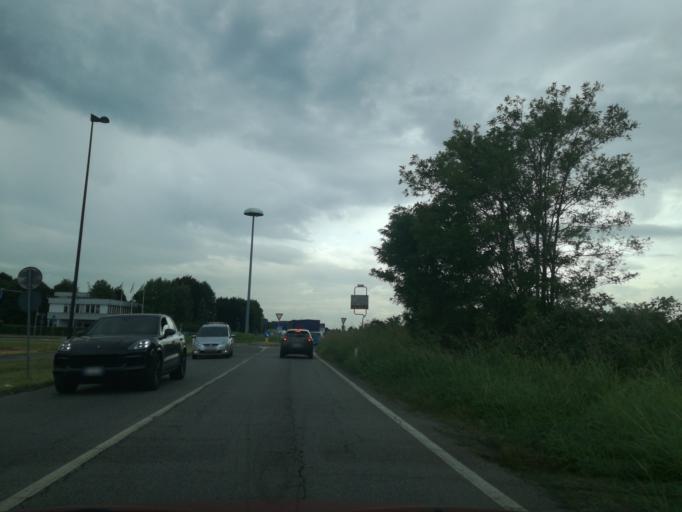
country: IT
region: Lombardy
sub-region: Provincia di Monza e Brianza
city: Ornago
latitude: 45.6083
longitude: 9.4193
